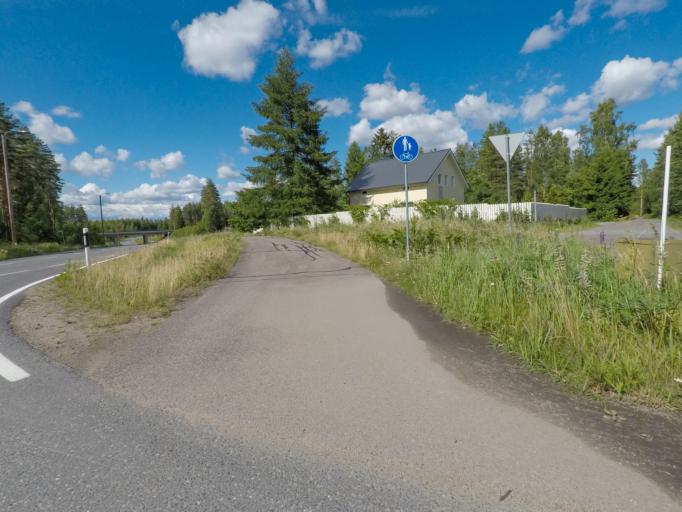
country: FI
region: South Karelia
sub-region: Lappeenranta
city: Joutseno
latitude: 61.0901
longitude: 28.3543
